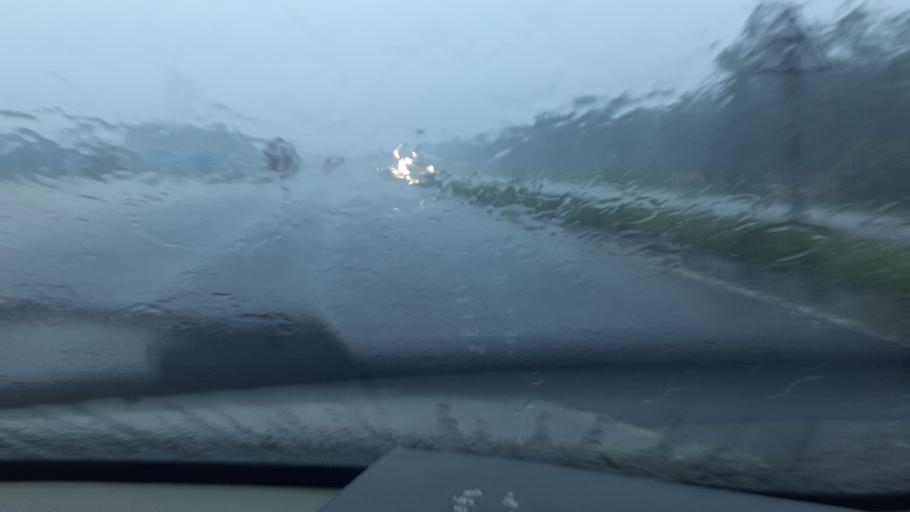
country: IN
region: Tamil Nadu
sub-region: Virudhunagar
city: Tiruttangal
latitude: 9.4600
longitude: 77.9322
